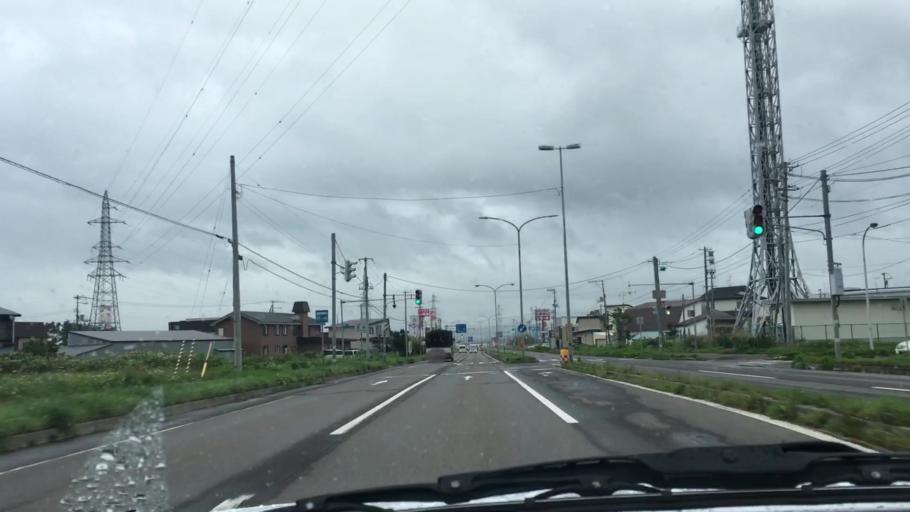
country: JP
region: Hokkaido
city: Nanae
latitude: 42.2585
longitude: 140.2781
